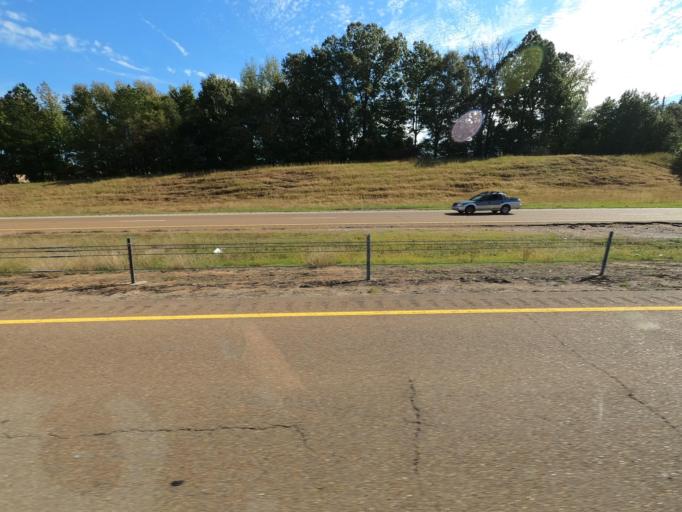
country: US
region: Tennessee
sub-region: Shelby County
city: Arlington
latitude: 35.2713
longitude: -89.6789
